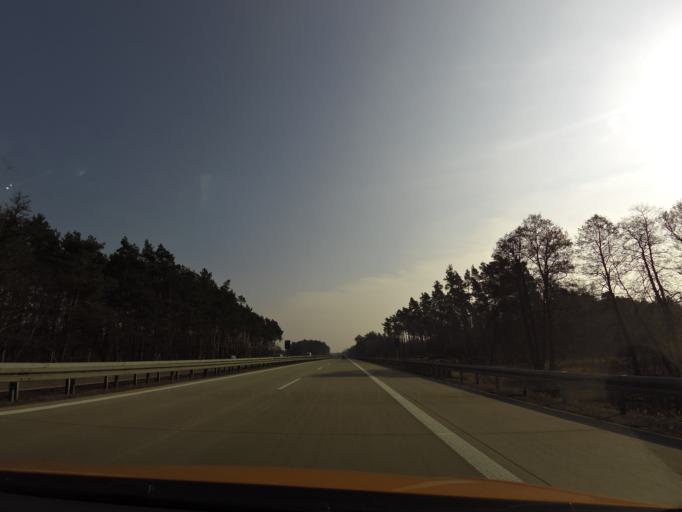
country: DE
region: Brandenburg
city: Briesen
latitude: 52.3321
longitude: 14.2594
